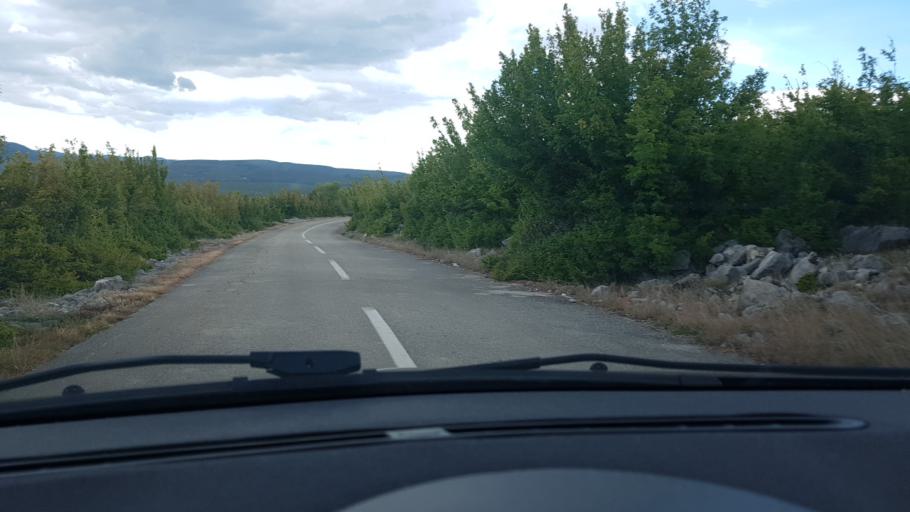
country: HR
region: Zadarska
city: Gracac
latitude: 44.1664
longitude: 15.8765
